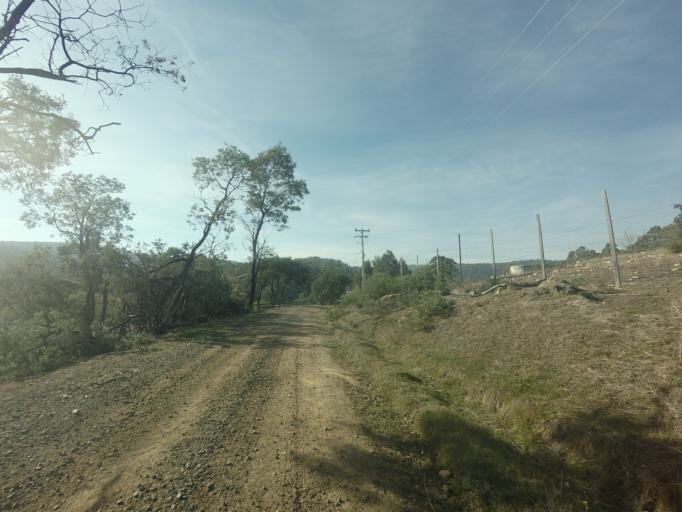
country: AU
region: Tasmania
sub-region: Sorell
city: Sorell
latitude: -42.5328
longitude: 147.4370
